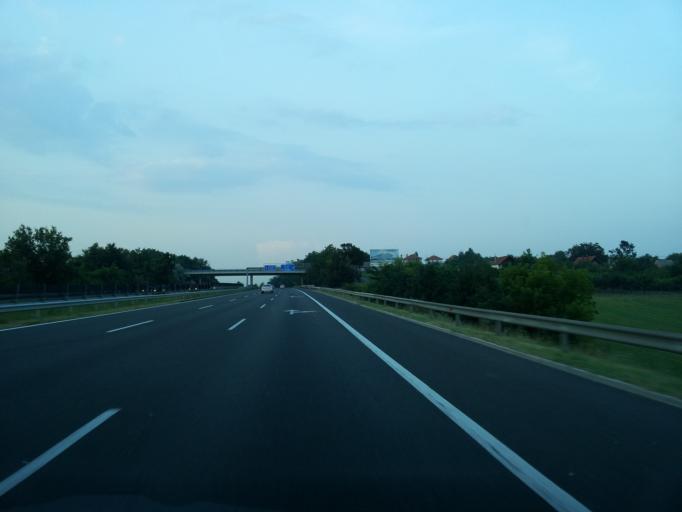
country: HU
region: Fejer
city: Martonvasar
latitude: 47.3254
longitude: 18.7696
